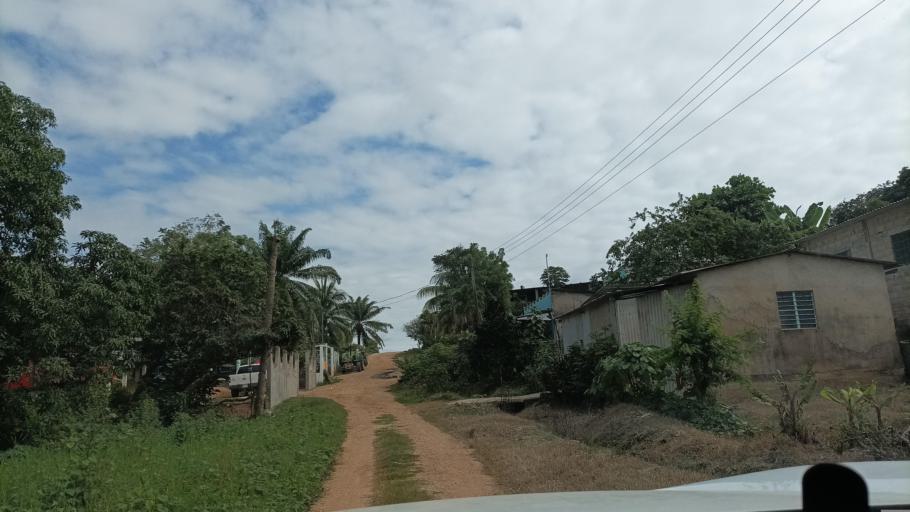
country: MX
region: Veracruz
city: Soconusco
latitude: 17.9615
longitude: -94.8152
